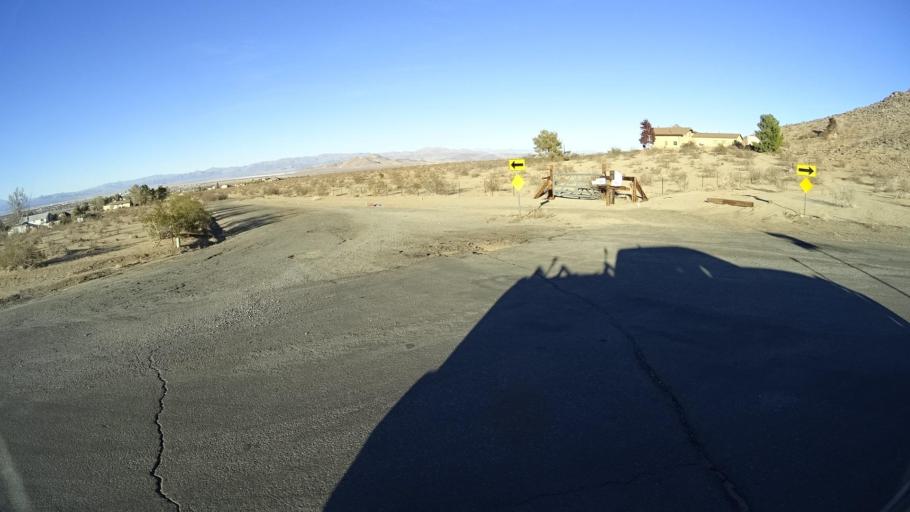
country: US
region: California
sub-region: Kern County
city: Ridgecrest
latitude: 35.5786
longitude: -117.6453
